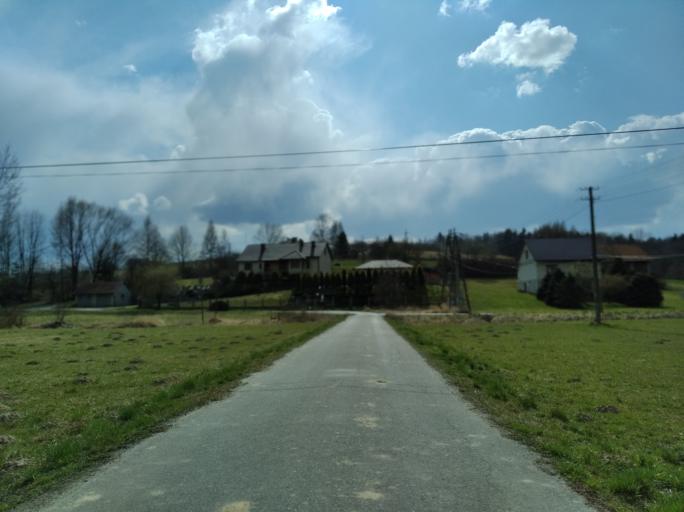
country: PL
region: Subcarpathian Voivodeship
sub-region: Powiat strzyzowski
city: Strzyzow
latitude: 49.9103
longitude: 21.7334
